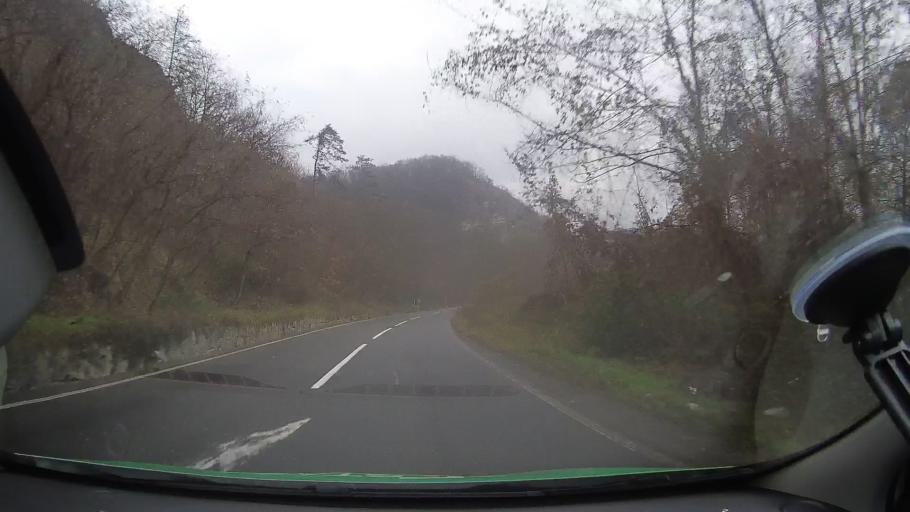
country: RO
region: Arad
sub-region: Comuna Gurahont
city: Gurahont
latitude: 46.2765
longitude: 22.3478
